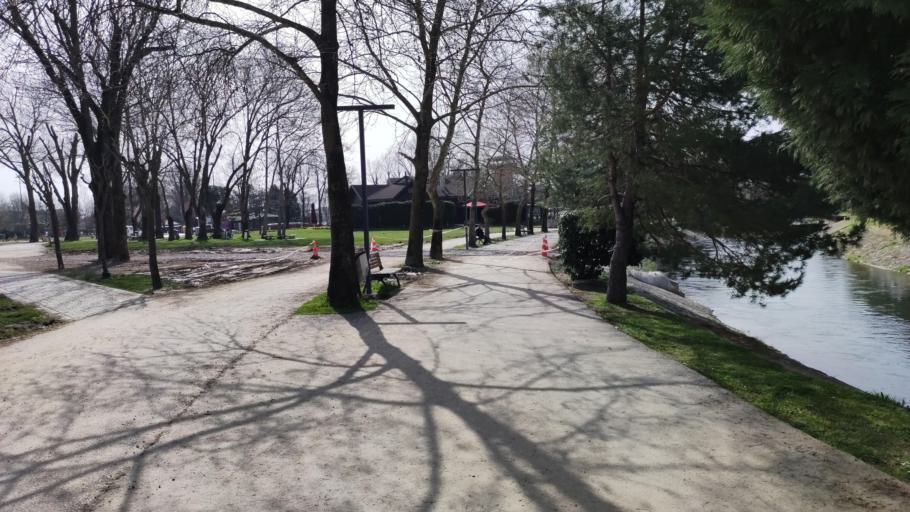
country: TR
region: Sakarya
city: Adapazari
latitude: 40.7738
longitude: 30.3867
